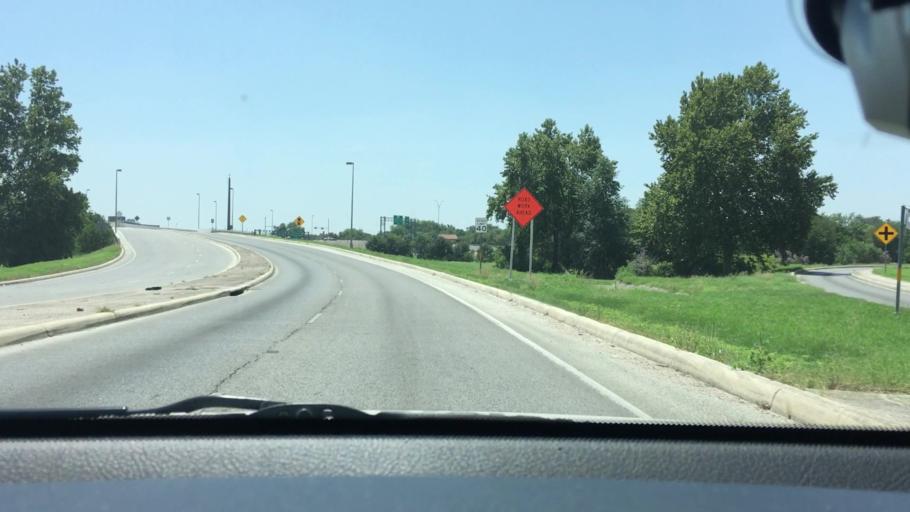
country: US
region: Texas
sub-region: Bexar County
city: Castle Hills
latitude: 29.5227
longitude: -98.5150
